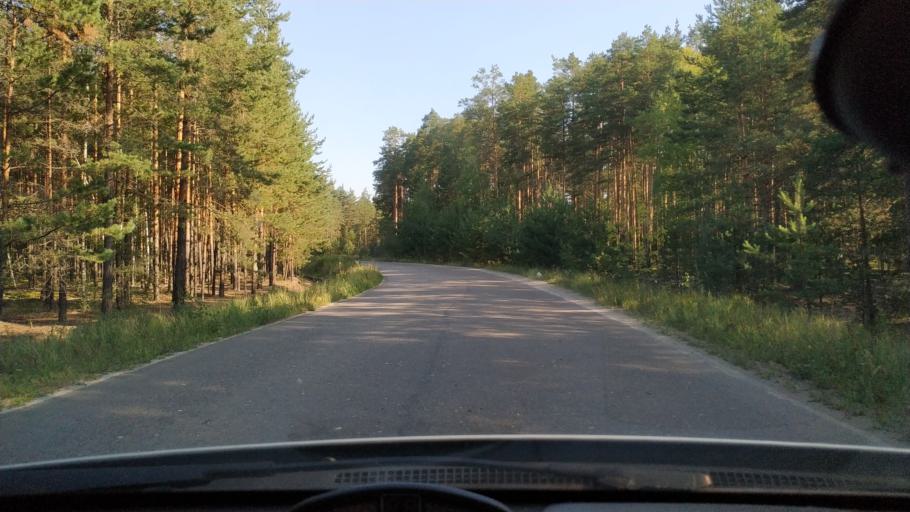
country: RU
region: Moskovskaya
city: Roshal'
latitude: 55.6521
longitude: 39.7997
